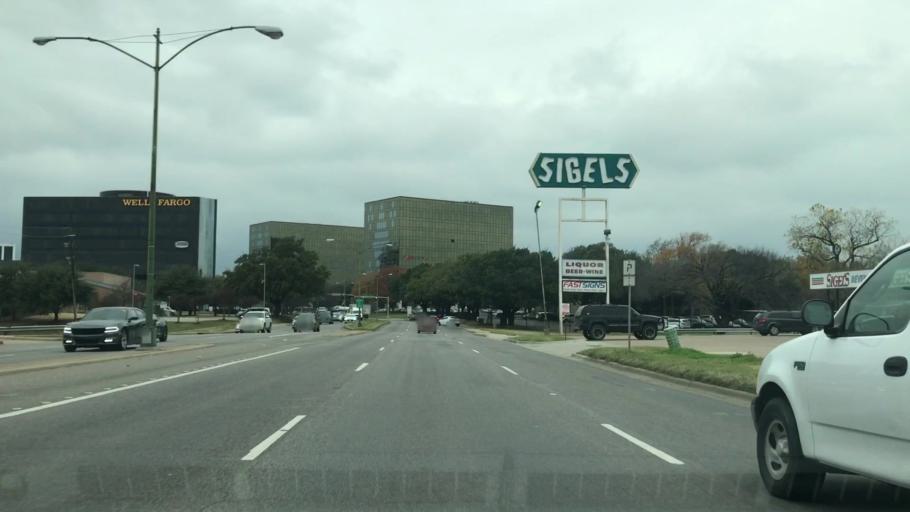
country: US
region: Texas
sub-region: Dallas County
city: University Park
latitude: 32.8223
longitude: -96.8613
